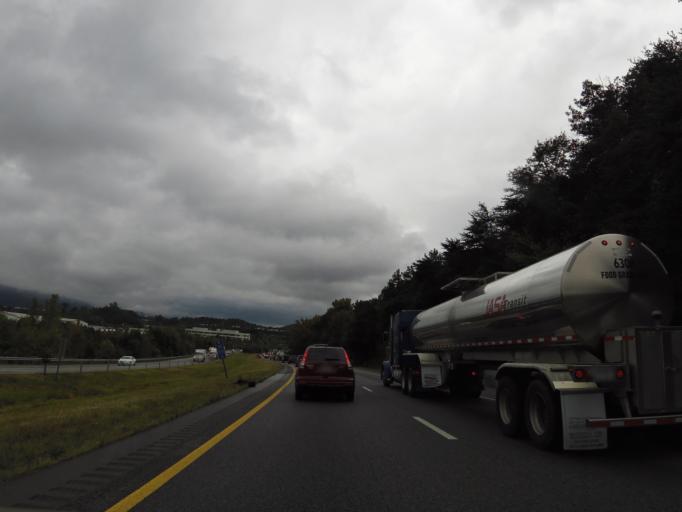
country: US
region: Tennessee
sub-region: Hamilton County
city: Lookout Mountain
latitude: 35.0150
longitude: -85.3871
